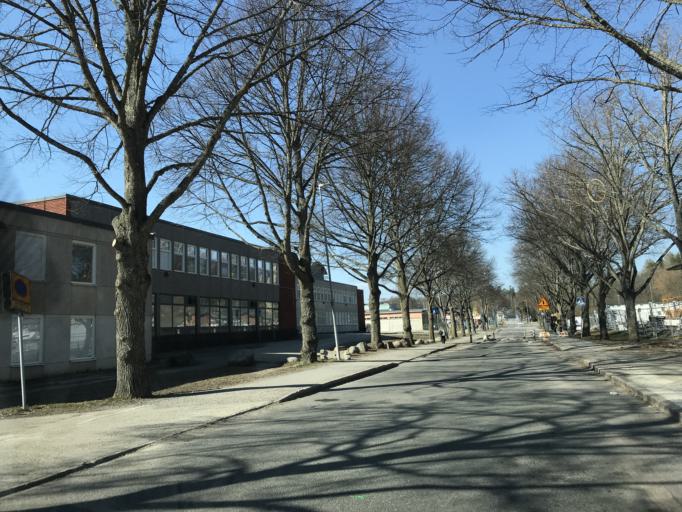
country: SE
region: Stockholm
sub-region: Sollentuna Kommun
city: Sollentuna
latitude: 59.4435
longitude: 17.9557
